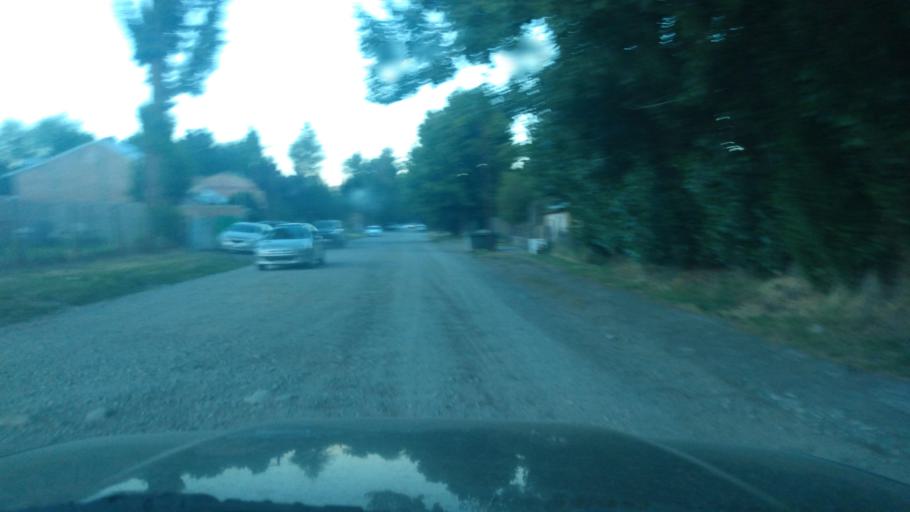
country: AR
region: Neuquen
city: Junin de los Andes
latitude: -39.9531
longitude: -71.0738
